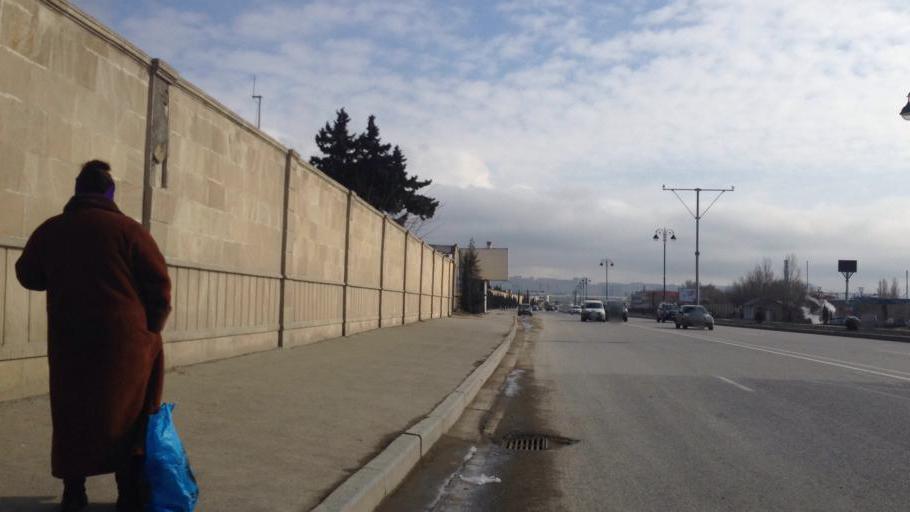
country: AZ
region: Baki
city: Baku
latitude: 40.3776
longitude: 49.9001
